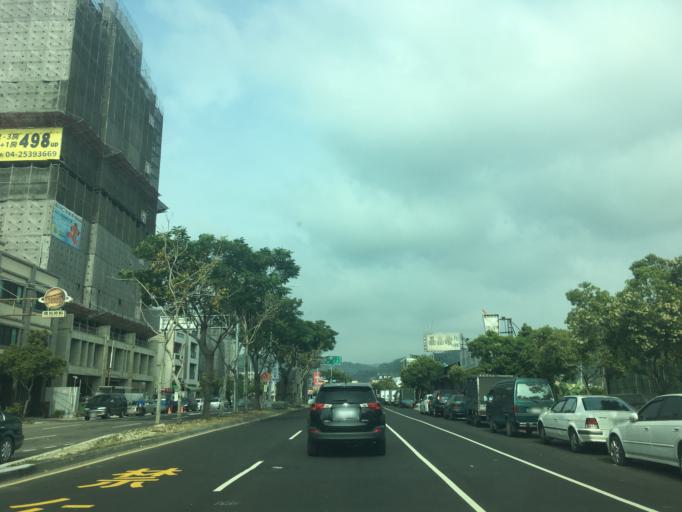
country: TW
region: Taiwan
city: Fengyuan
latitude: 24.2367
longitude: 120.7186
